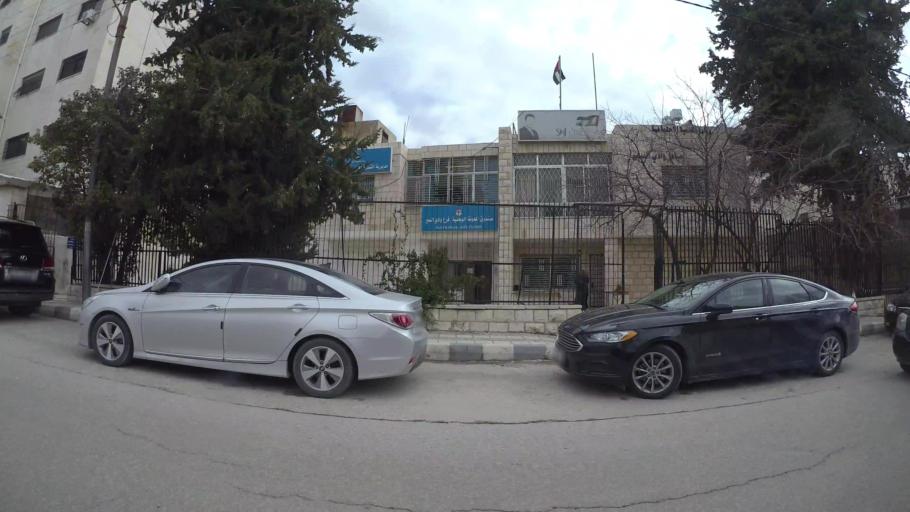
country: JO
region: Amman
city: Wadi as Sir
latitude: 31.9495
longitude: 35.8387
